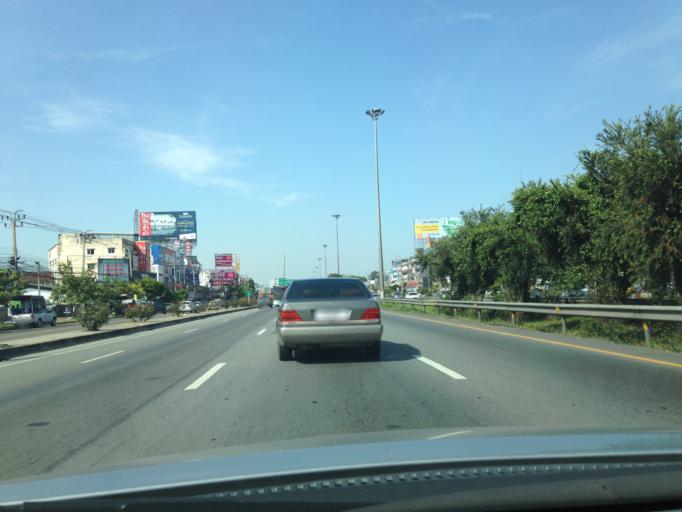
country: TH
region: Nonthaburi
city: Bang Yai
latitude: 13.8451
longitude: 100.4126
